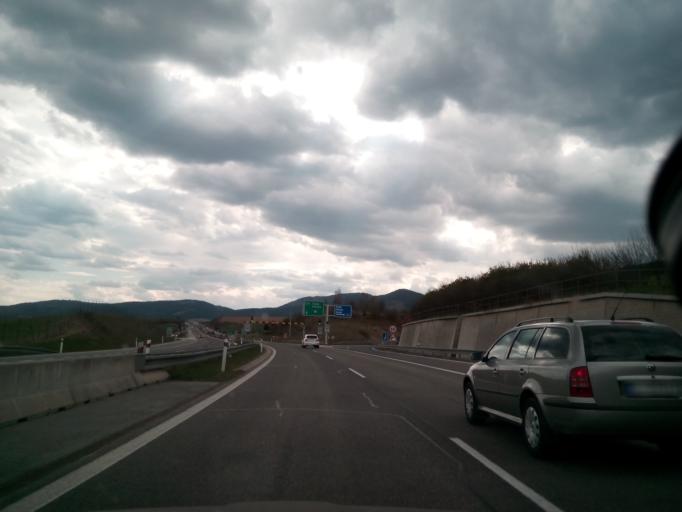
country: SK
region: Kosicky
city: Krompachy
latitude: 49.0136
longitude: 20.9440
